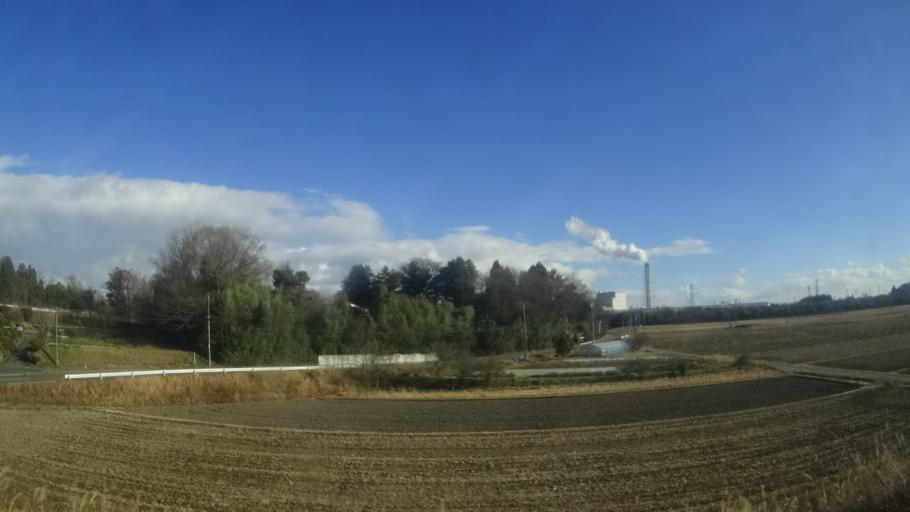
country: JP
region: Miyagi
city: Marumori
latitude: 37.8536
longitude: 140.9294
